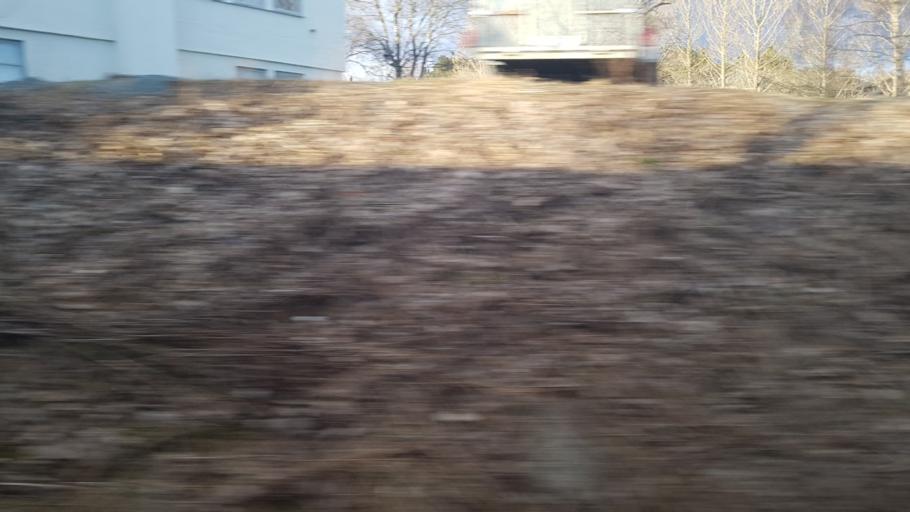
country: NO
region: Sor-Trondelag
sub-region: Trondheim
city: Trondheim
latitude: 63.4282
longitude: 10.5318
